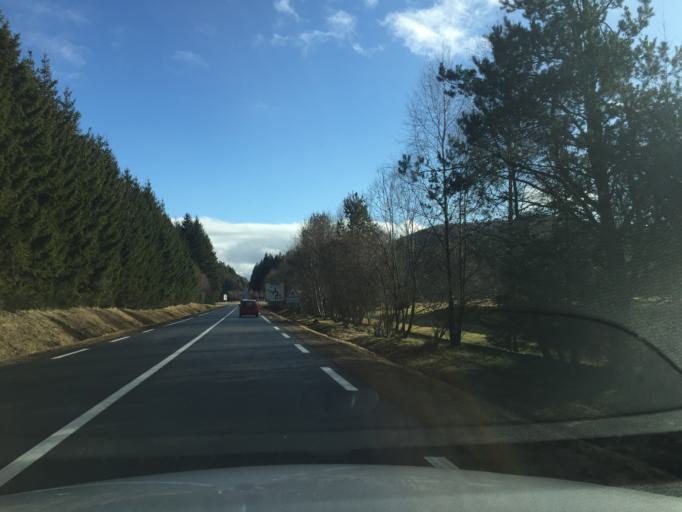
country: FR
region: Auvergne
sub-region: Departement du Puy-de-Dome
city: Saint-Ours
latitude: 45.8149
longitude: 2.9487
